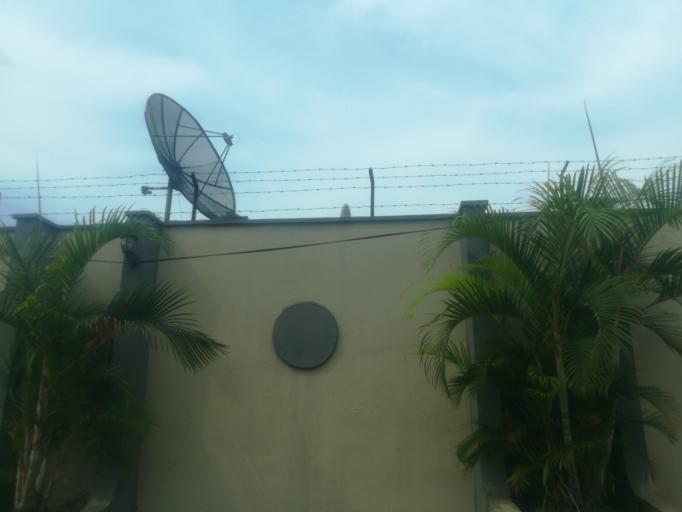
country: NG
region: Oyo
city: Ibadan
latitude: 7.4237
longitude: 3.9120
